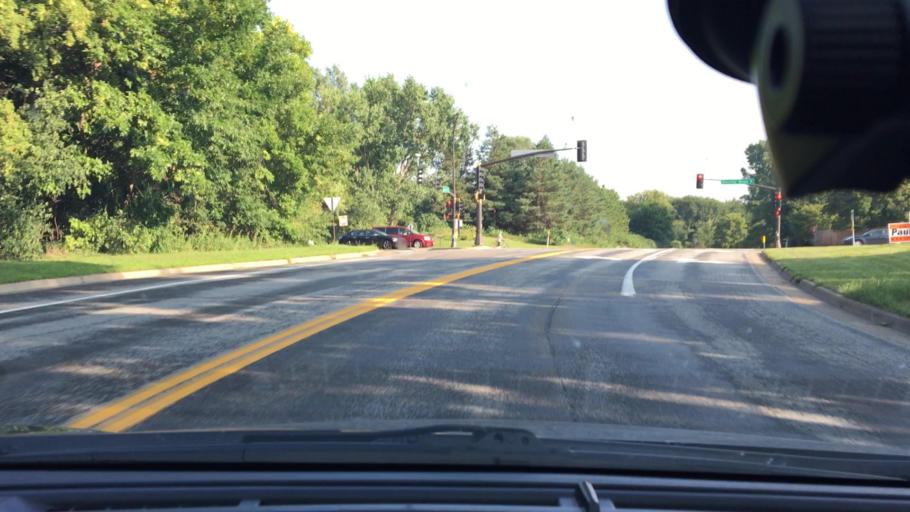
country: US
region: Minnesota
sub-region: Hennepin County
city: Plymouth
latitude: 45.0331
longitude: -93.4344
